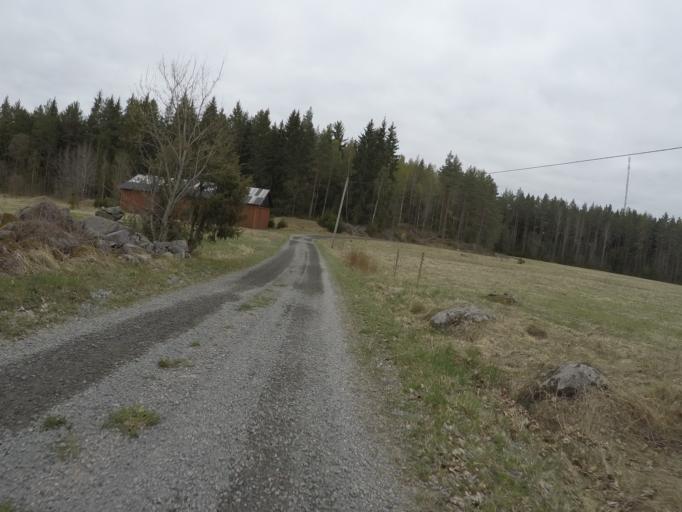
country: SE
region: Soedermanland
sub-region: Eskilstuna Kommun
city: Kvicksund
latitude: 59.3984
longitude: 16.3067
